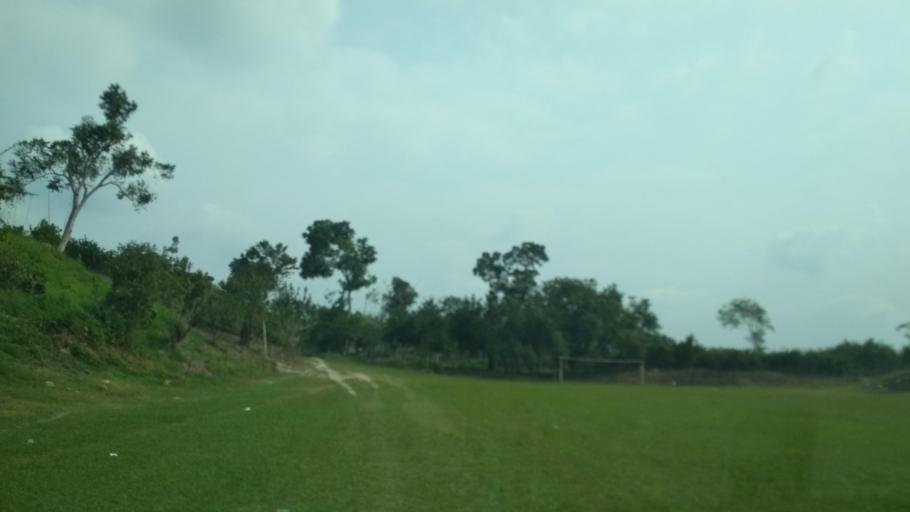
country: MM
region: Kayah
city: Loikaw
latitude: 20.2116
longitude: 97.2846
